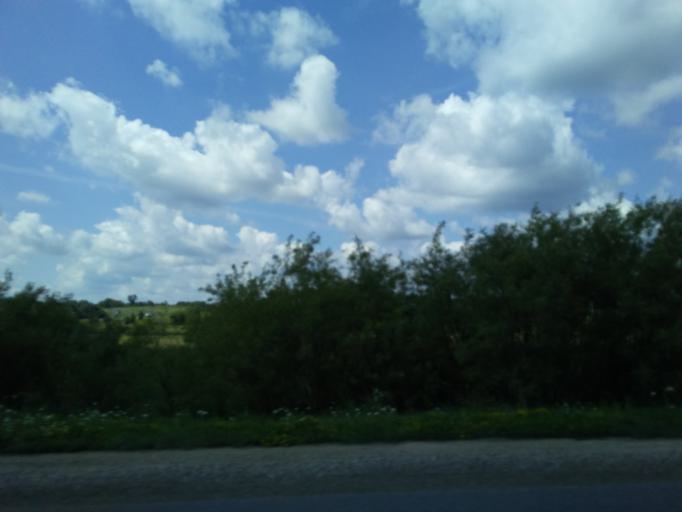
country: US
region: Wisconsin
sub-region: Dane County
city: Verona
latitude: 42.9896
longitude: -89.5701
